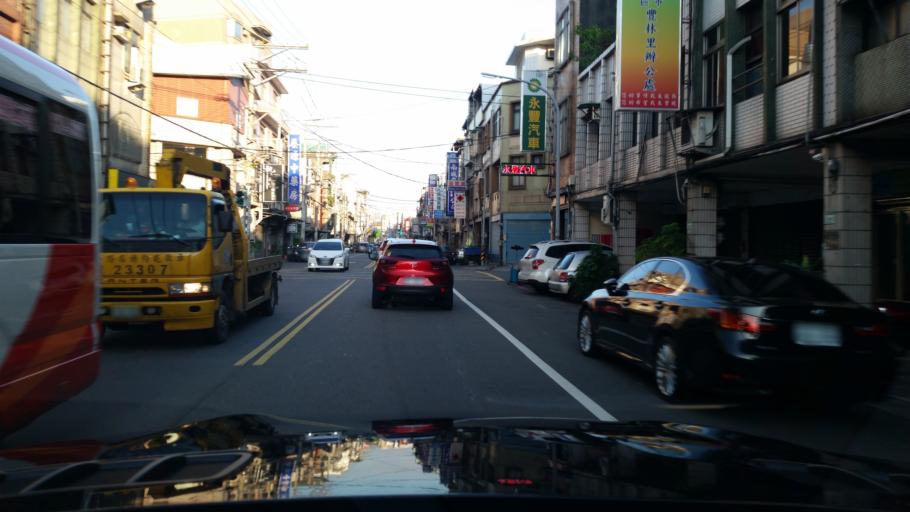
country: TW
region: Taiwan
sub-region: Taoyuan
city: Taoyuan
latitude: 24.9851
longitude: 121.3080
